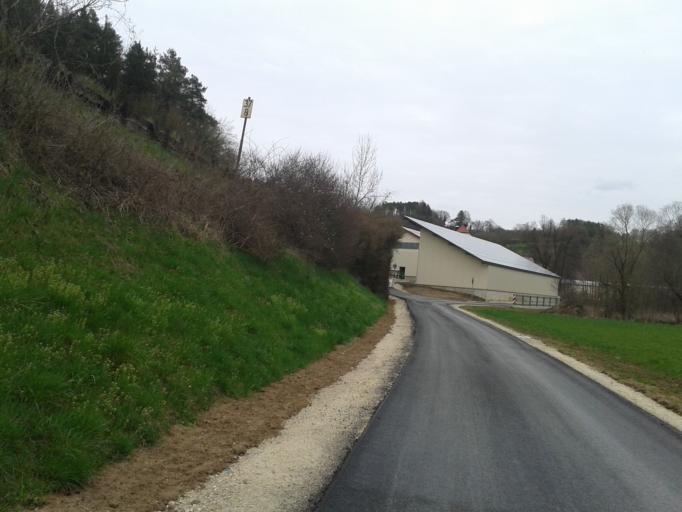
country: DE
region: Bavaria
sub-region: Upper Palatinate
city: Weigendorf
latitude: 49.5001
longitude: 11.5653
